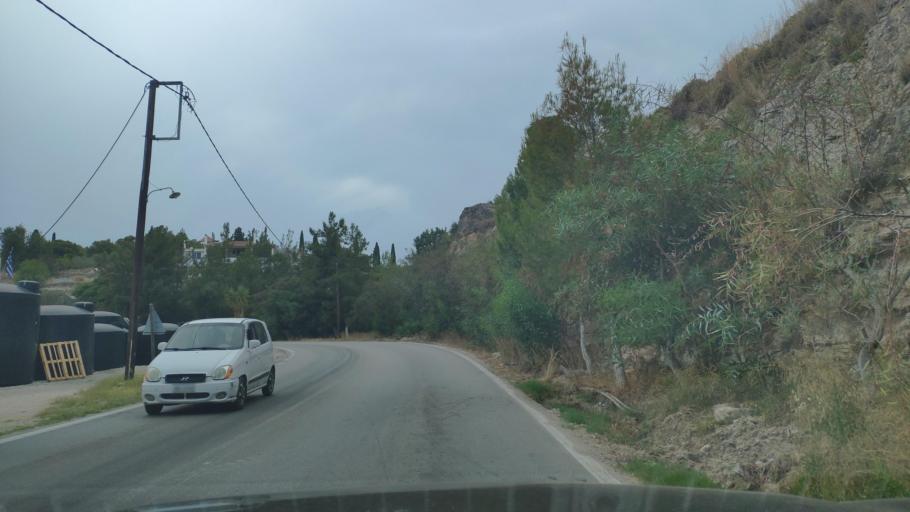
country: GR
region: Peloponnese
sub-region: Nomos Argolidos
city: Kranidi
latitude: 37.3829
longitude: 23.1542
